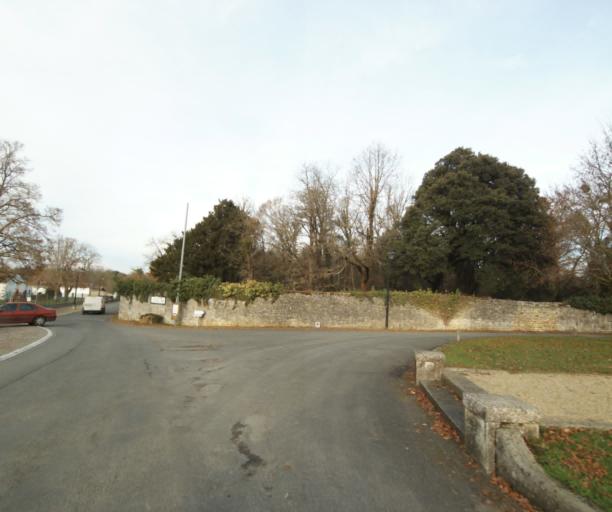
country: FR
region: Poitou-Charentes
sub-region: Departement de la Charente-Maritime
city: Saint-Hilaire-de-Villefranche
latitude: 45.8188
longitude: -0.5690
